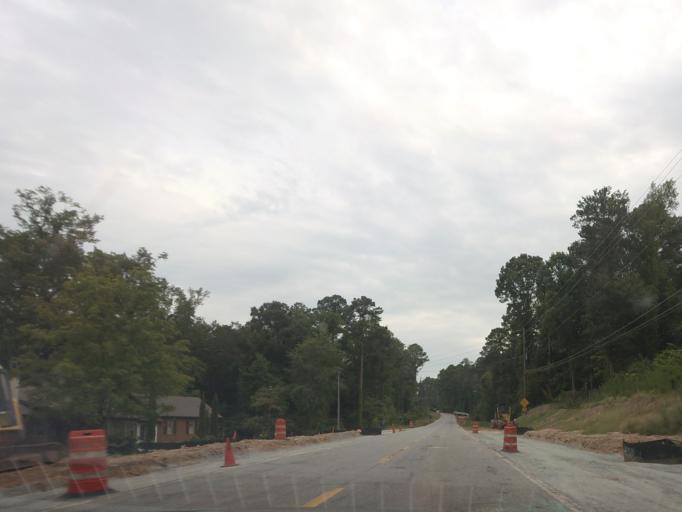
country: US
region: Georgia
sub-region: Bibb County
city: Macon
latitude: 32.8842
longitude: -83.6955
